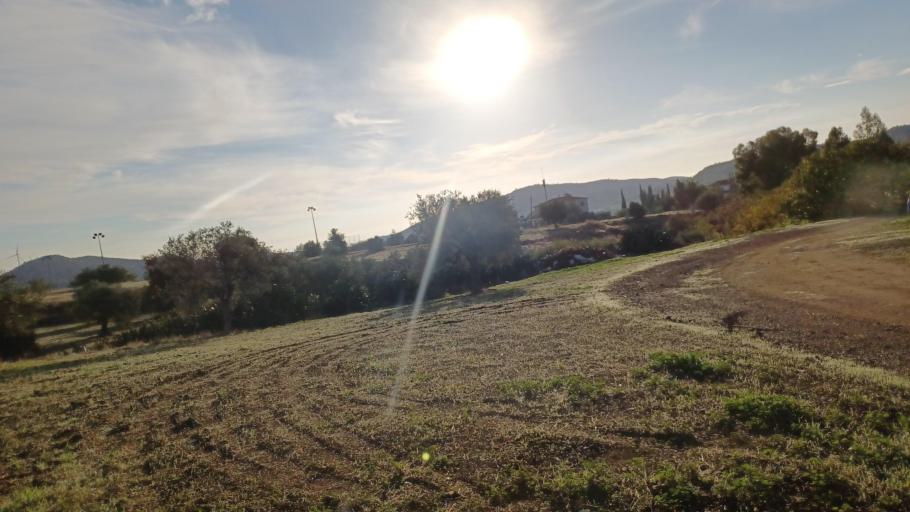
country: CY
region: Larnaka
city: Mosfiloti
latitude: 34.9277
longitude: 33.4330
